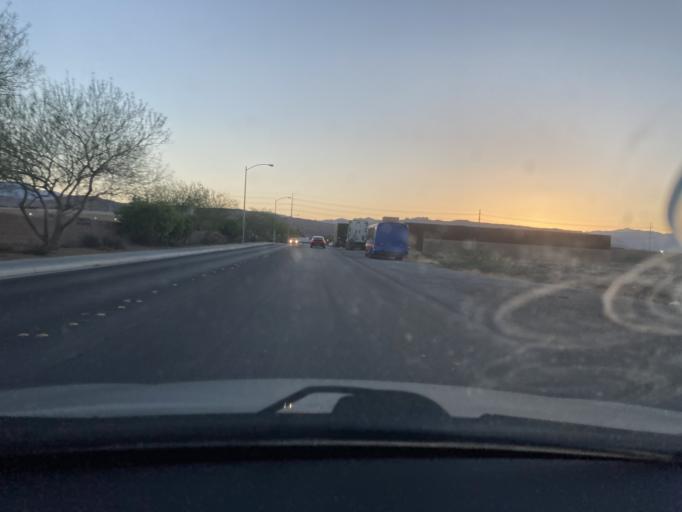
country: US
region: Nevada
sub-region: Clark County
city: Enterprise
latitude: 36.0592
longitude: -115.2749
